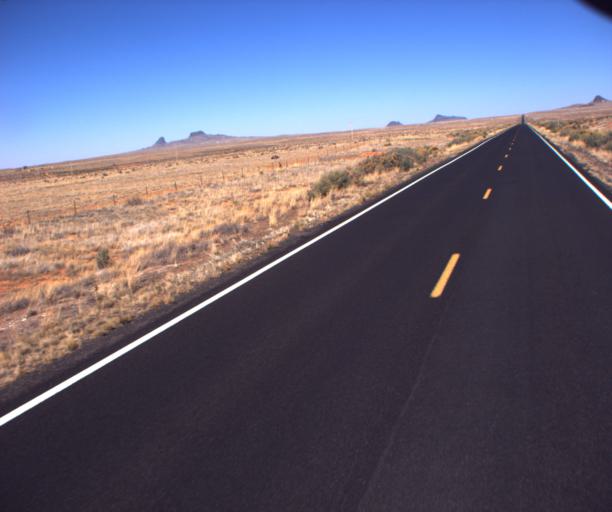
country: US
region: Arizona
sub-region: Navajo County
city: Dilkon
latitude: 35.3432
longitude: -110.4240
